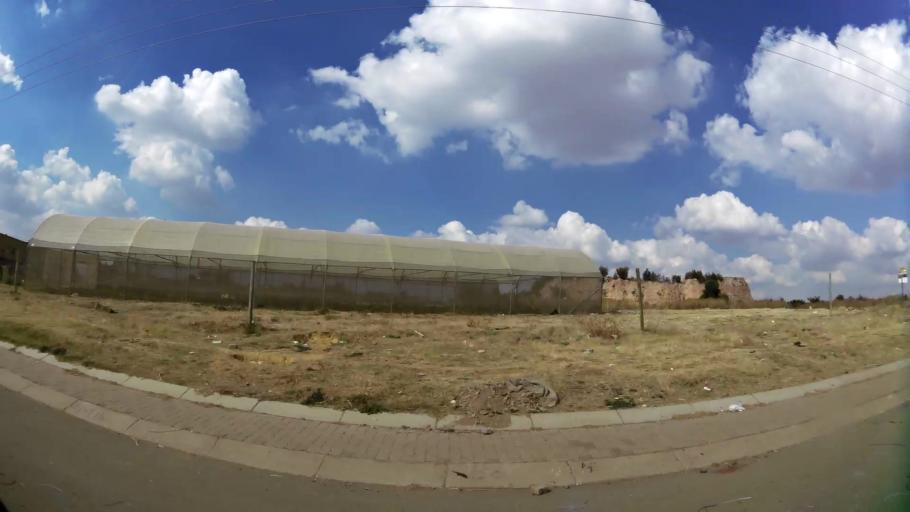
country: ZA
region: Gauteng
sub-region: City of Johannesburg Metropolitan Municipality
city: Roodepoort
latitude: -26.1847
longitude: 27.8460
